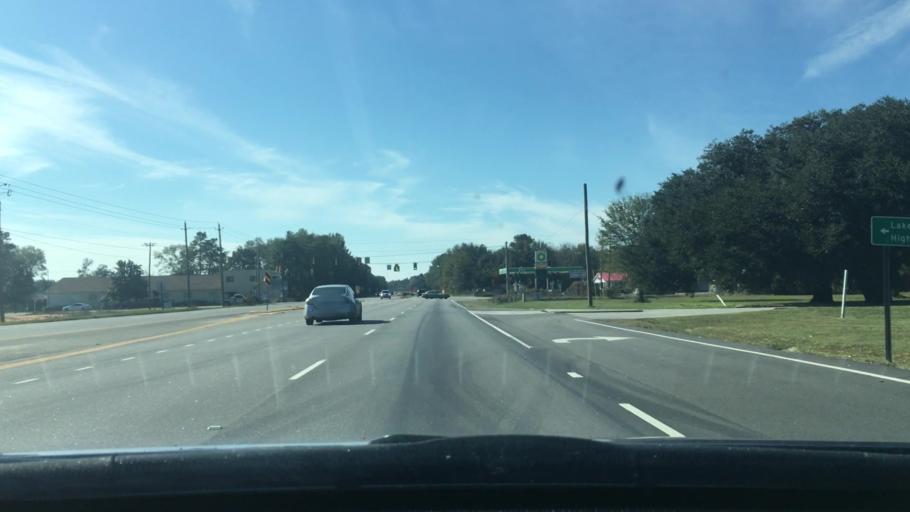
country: US
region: South Carolina
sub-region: Sumter County
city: Lakewood
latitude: 33.8685
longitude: -80.3574
